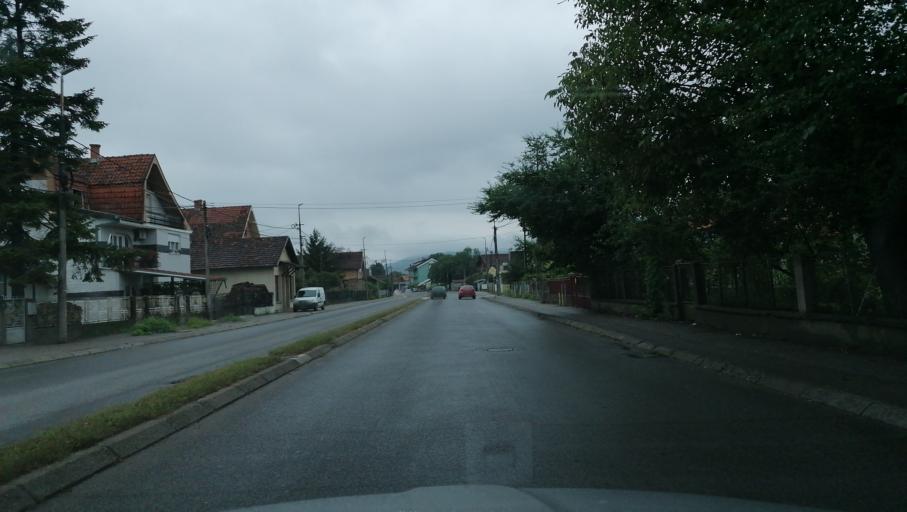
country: RS
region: Central Serbia
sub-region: Rasinski Okrug
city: Krusevac
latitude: 43.5836
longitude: 21.3060
